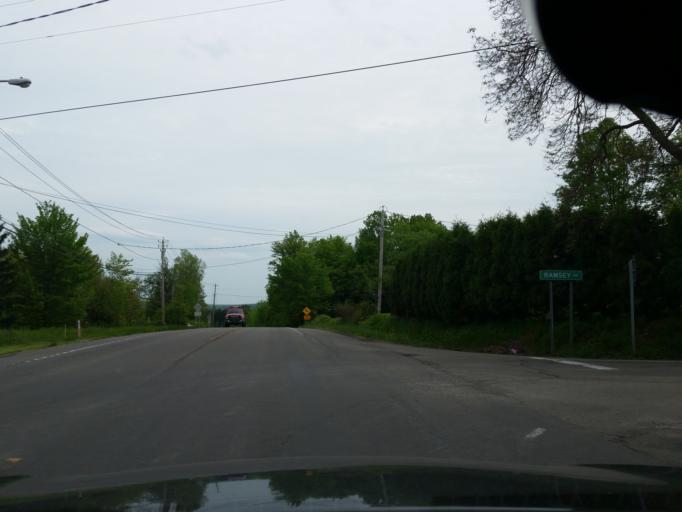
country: US
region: New York
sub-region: Chautauqua County
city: Lakewood
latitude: 42.1402
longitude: -79.4005
